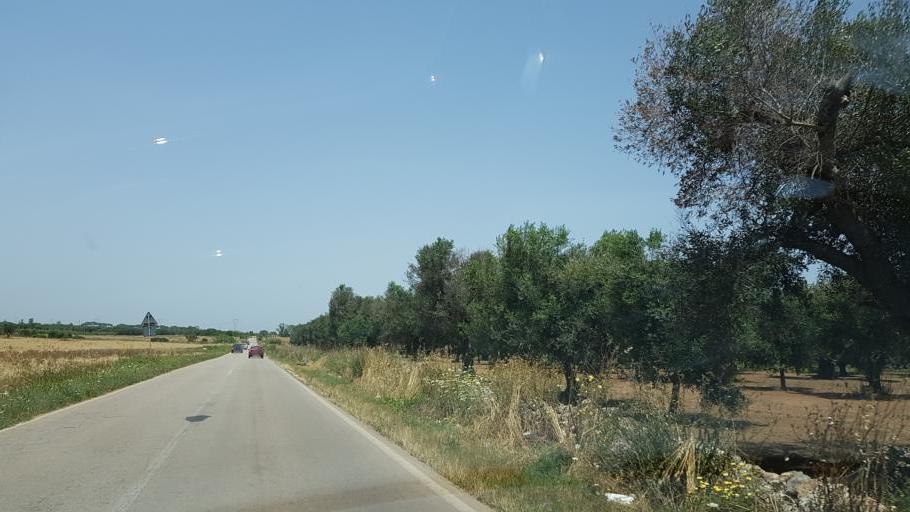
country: IT
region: Apulia
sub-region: Provincia di Lecce
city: Porto Cesareo
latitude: 40.3296
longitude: 17.8528
